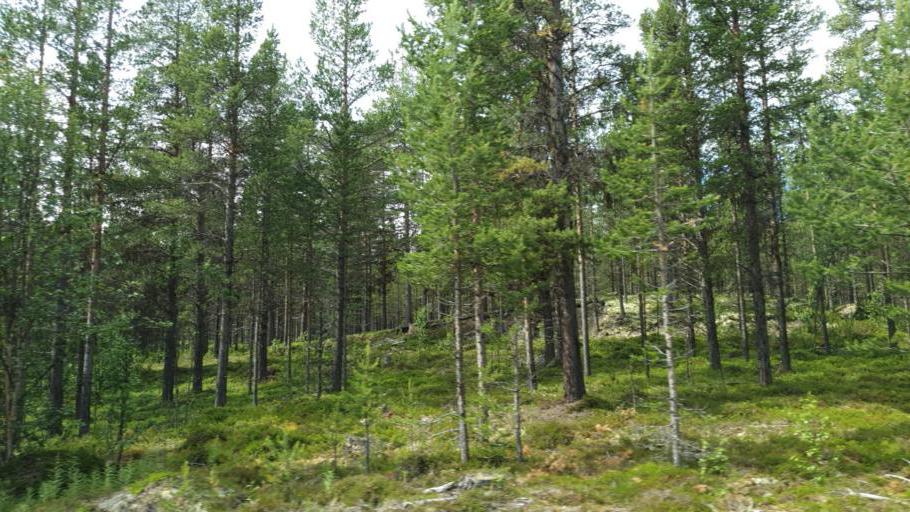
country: NO
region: Oppland
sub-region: Vaga
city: Vagamo
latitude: 61.6966
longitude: 9.0601
